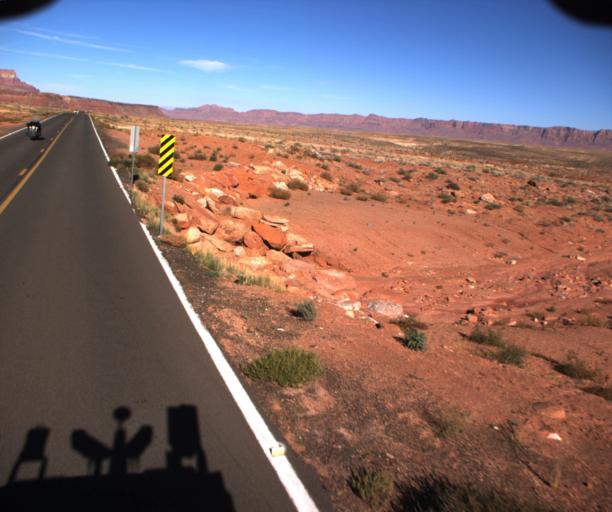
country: US
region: Arizona
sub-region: Coconino County
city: LeChee
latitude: 36.7064
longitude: -111.7850
